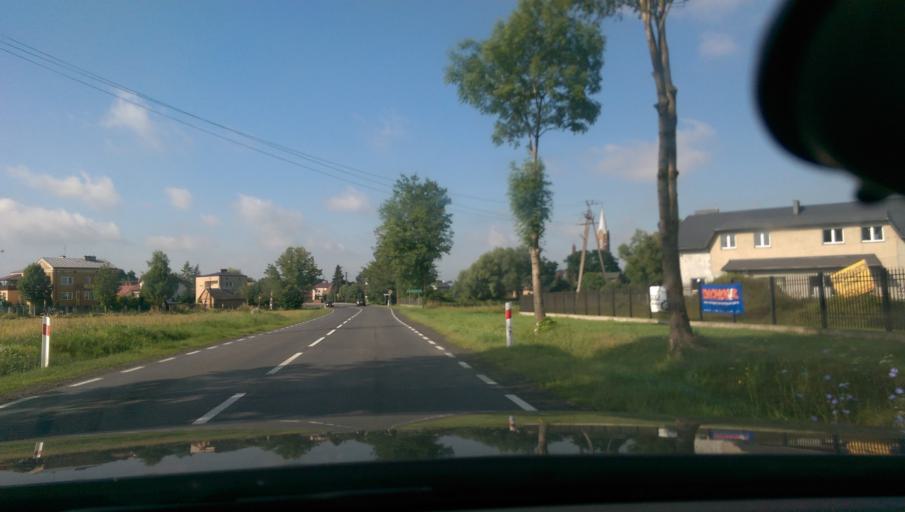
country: PL
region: Masovian Voivodeship
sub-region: Powiat plonski
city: Sochocin
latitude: 52.6919
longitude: 20.4753
